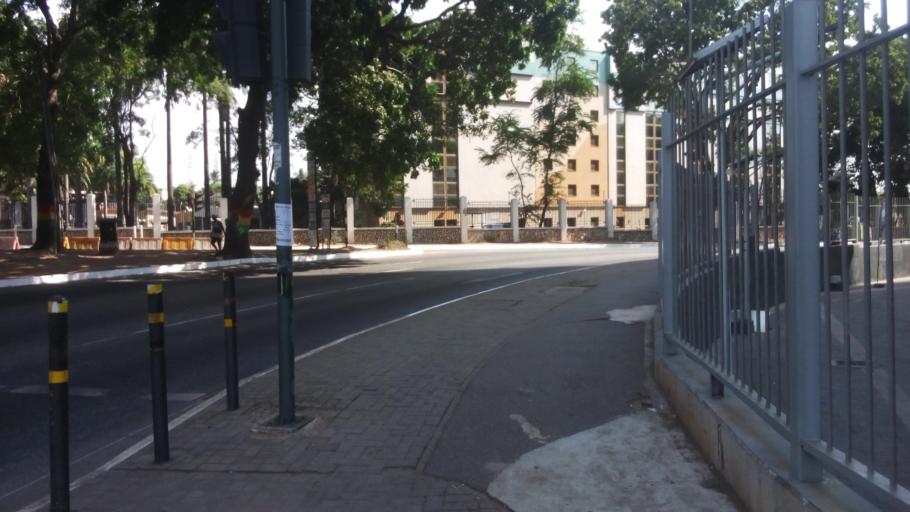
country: GH
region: Greater Accra
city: Accra
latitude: 5.5521
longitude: -0.2040
